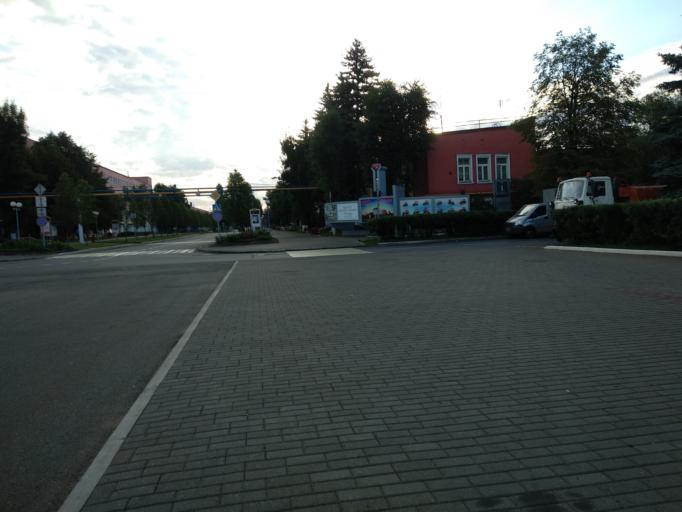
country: BY
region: Minsk
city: Minsk
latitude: 53.8908
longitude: 27.6187
